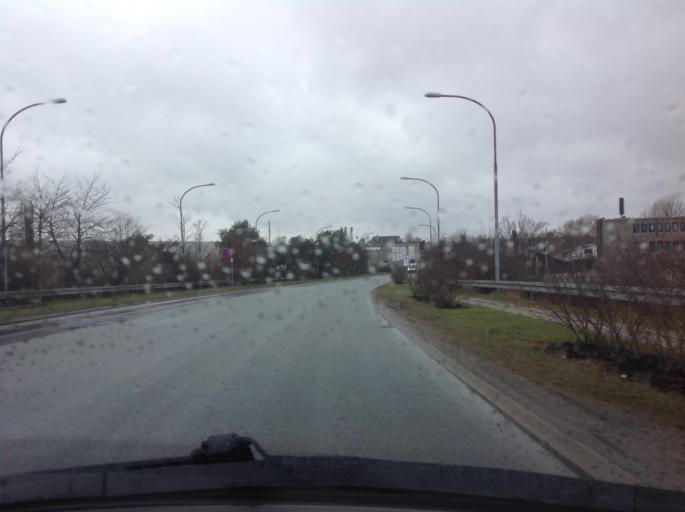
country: DK
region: Capital Region
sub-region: Ishoj Kommune
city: Ishoj
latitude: 55.6169
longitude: 12.3254
